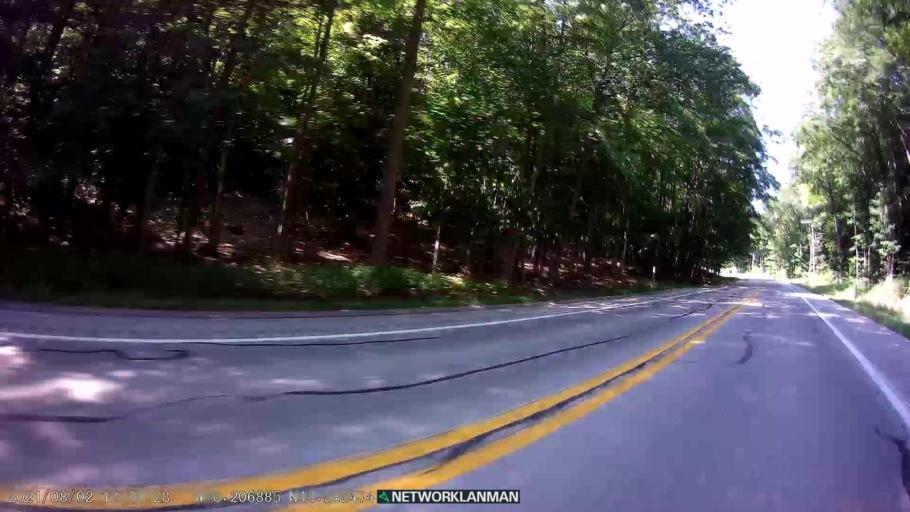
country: US
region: Michigan
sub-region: Benzie County
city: Frankfort
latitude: 44.5858
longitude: -86.2067
